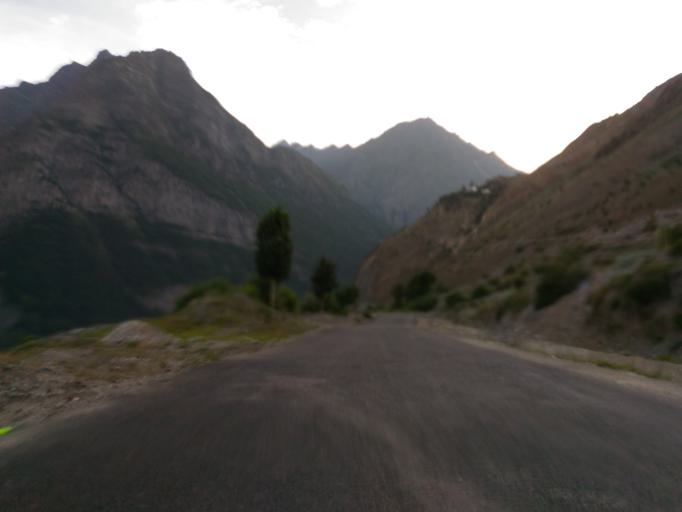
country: IN
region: Himachal Pradesh
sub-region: Lahul and Spiti
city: Kyelang
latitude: 32.5129
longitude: 77.0102
